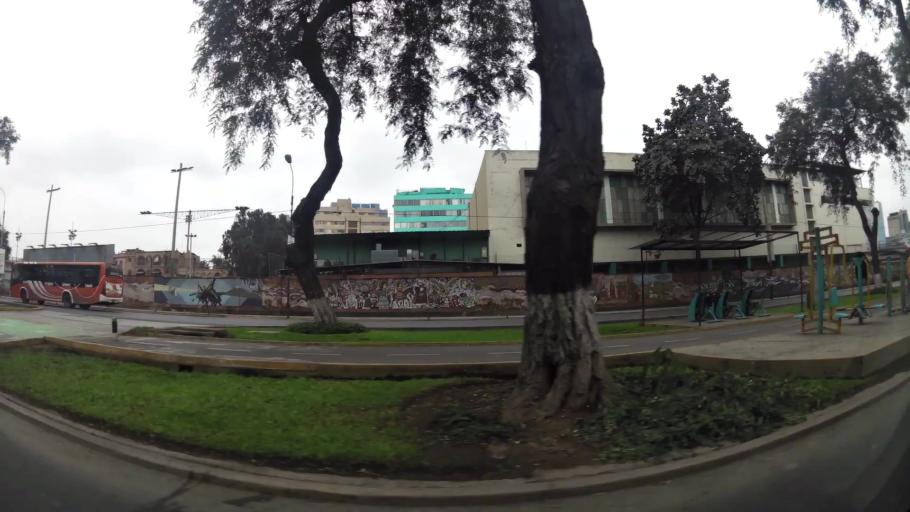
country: PE
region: Lima
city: Lima
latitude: -12.0664
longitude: -77.0393
